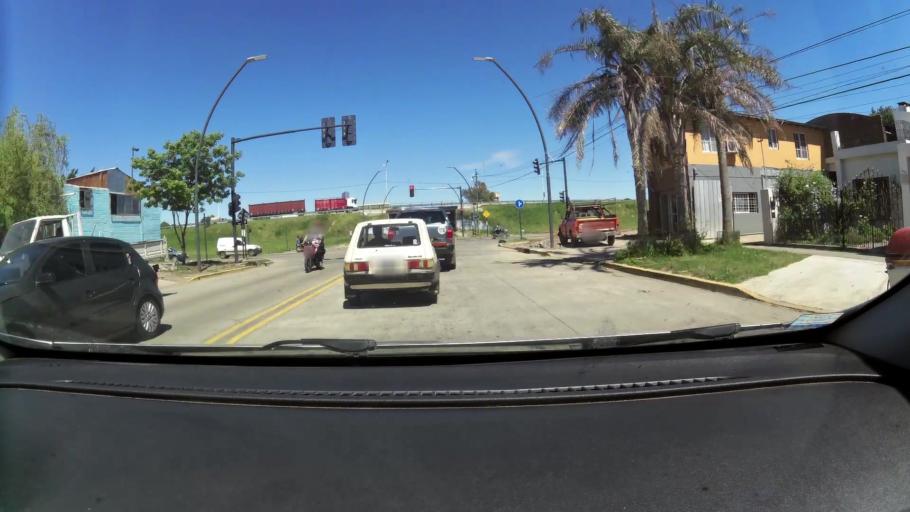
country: AR
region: Santa Fe
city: Perez
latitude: -32.9660
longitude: -60.7181
